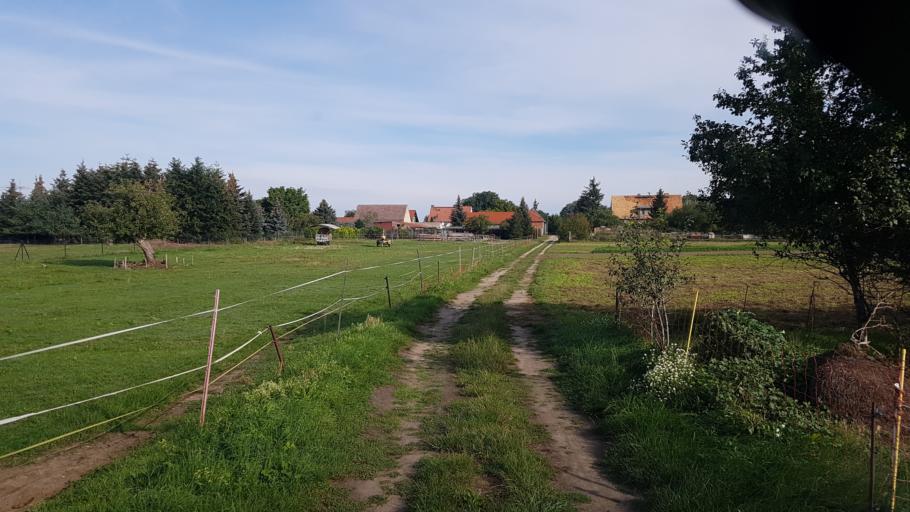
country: DE
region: Brandenburg
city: Finsterwalde
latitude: 51.6613
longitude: 13.6817
